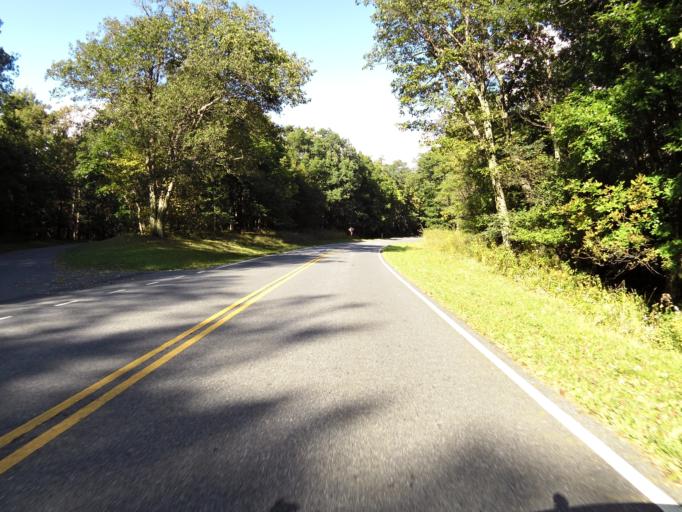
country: US
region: Virginia
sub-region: Page County
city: Stanley
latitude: 38.5324
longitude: -78.4228
